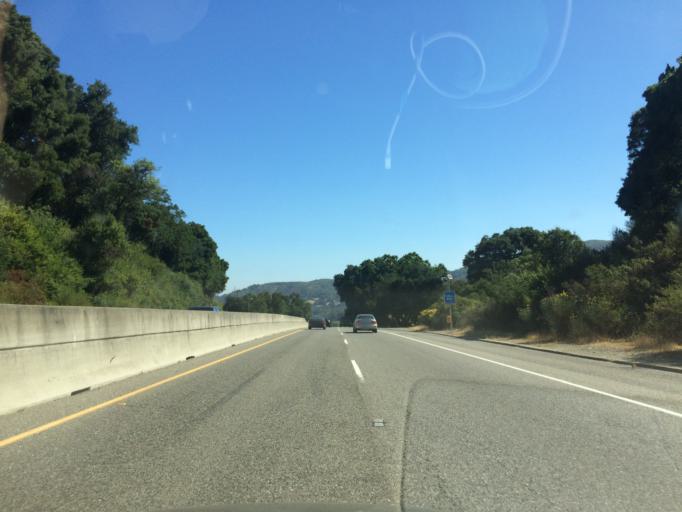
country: US
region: California
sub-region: Santa Clara County
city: Lexington Hills
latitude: 37.1786
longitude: -121.9951
